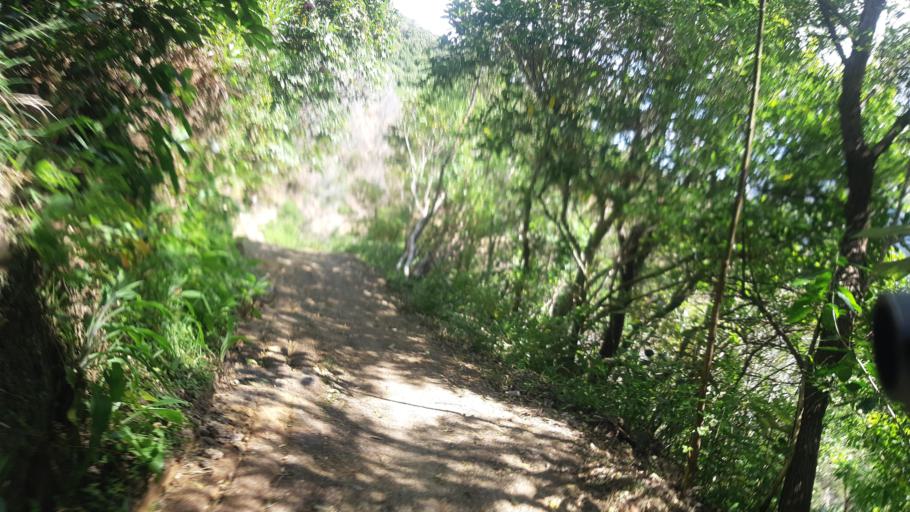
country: NZ
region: Marlborough
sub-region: Marlborough District
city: Picton
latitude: -41.2669
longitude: 174.0277
